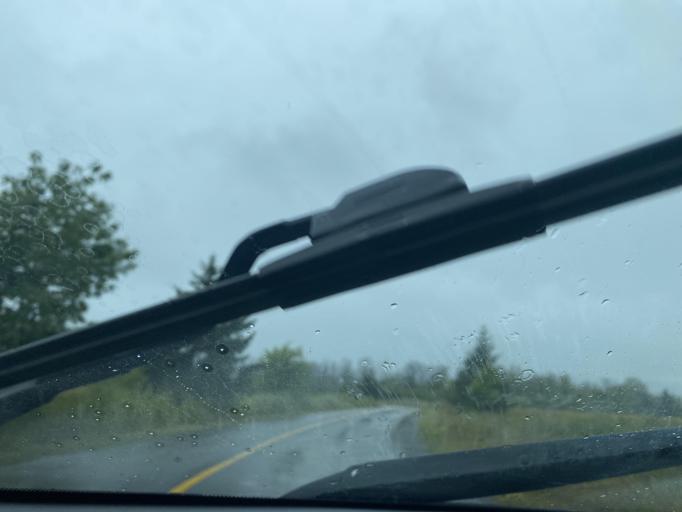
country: CA
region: Quebec
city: Baie-D'Urfe
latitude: 45.4645
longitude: -73.9227
